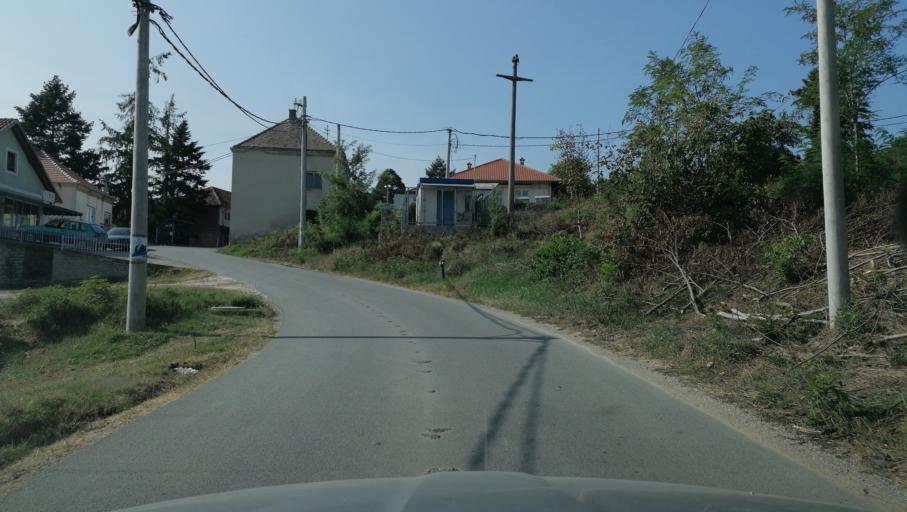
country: RS
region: Central Serbia
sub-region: Belgrade
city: Sopot
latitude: 44.5842
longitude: 20.6098
